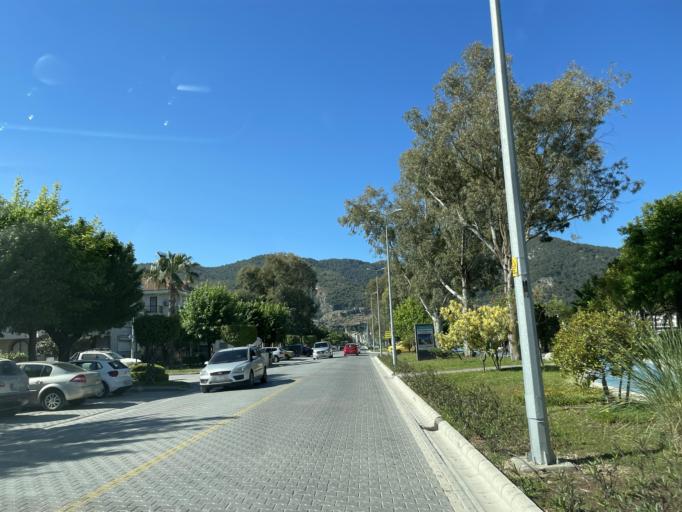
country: TR
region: Mugla
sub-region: Fethiye
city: Fethiye
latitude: 36.6297
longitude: 29.1177
